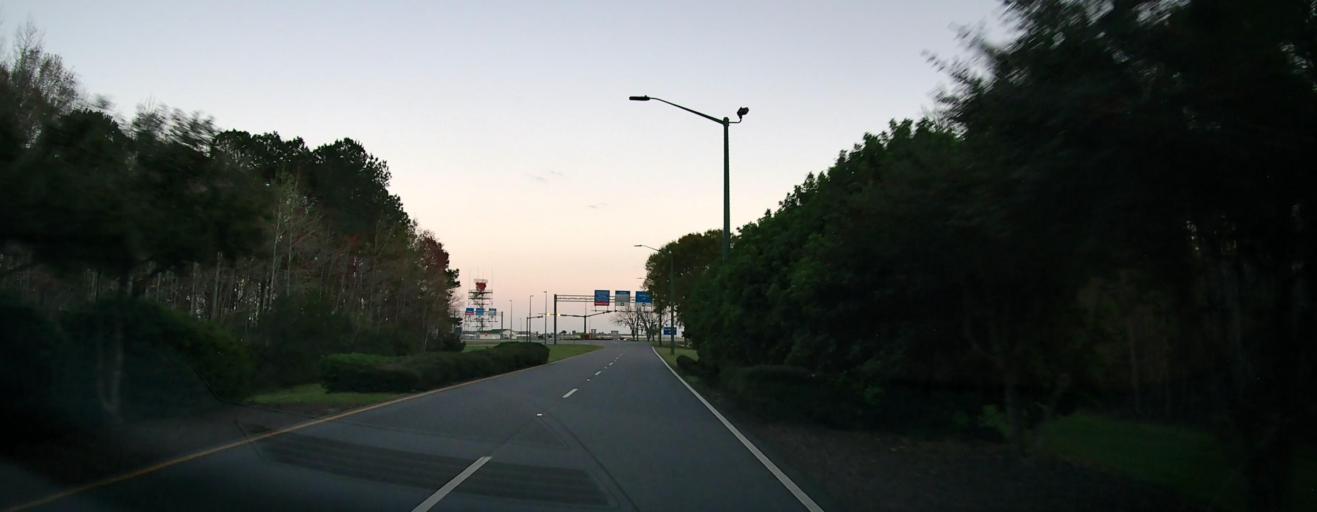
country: US
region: Georgia
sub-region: Chatham County
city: Pooler
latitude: 32.1351
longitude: -81.2161
